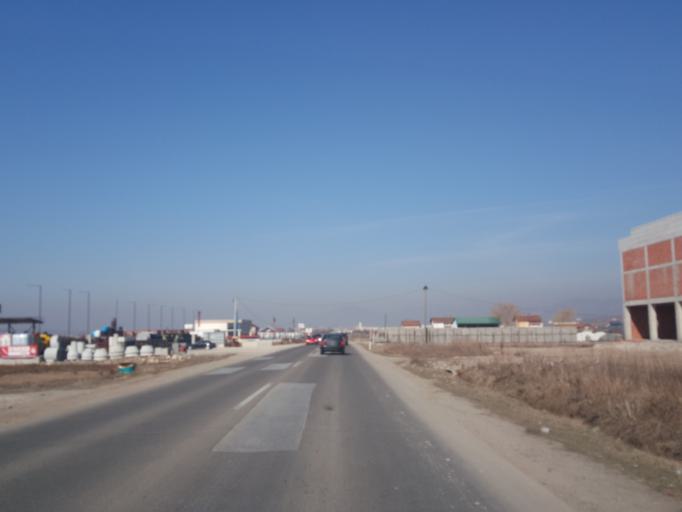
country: XK
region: Mitrovica
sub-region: Vushtrri
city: Vushtrri
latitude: 42.7907
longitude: 21.0046
